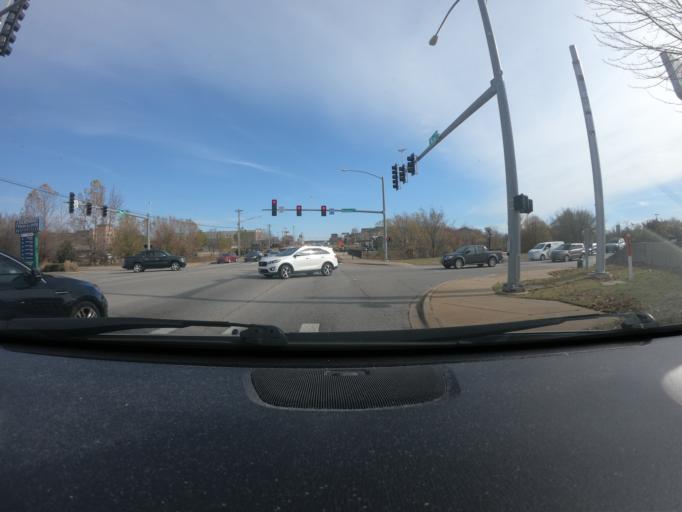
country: US
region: Arkansas
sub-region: Benton County
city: Bentonville
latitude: 36.3352
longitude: -94.1910
